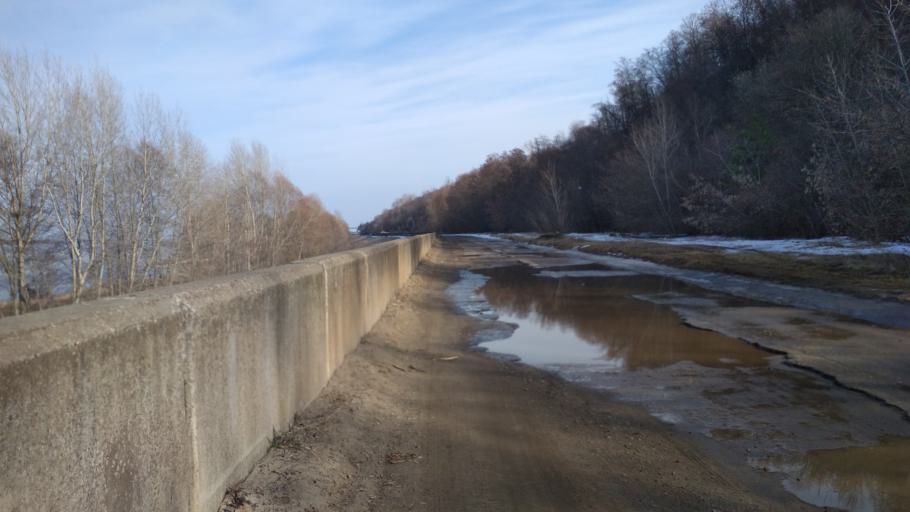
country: RU
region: Chuvashia
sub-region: Cheboksarskiy Rayon
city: Cheboksary
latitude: 56.1467
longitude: 47.3056
